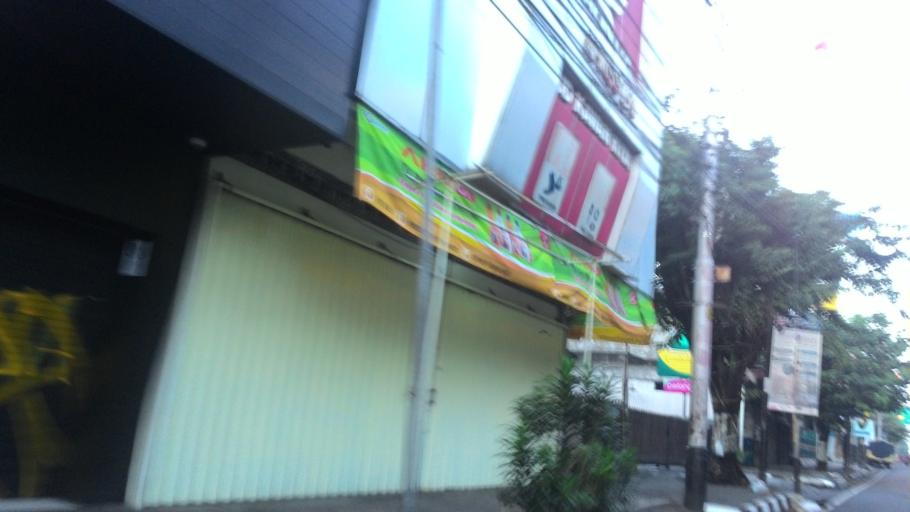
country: ID
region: Daerah Istimewa Yogyakarta
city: Yogyakarta
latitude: -7.7832
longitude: 110.3900
